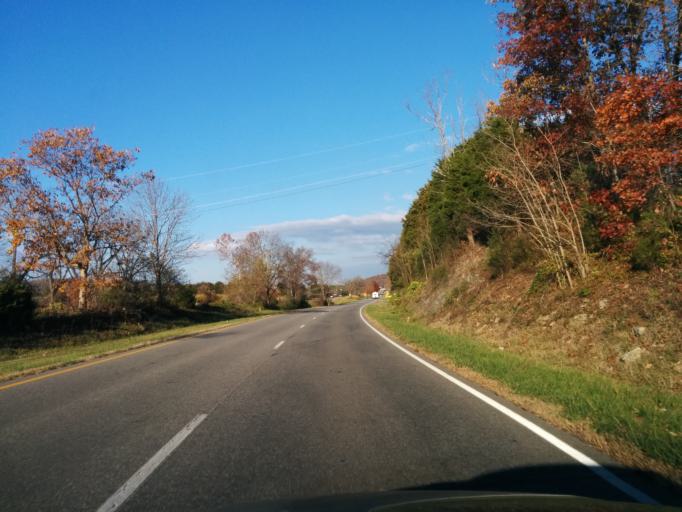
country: US
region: Virginia
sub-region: Rockbridge County
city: East Lexington
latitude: 37.8243
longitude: -79.3879
